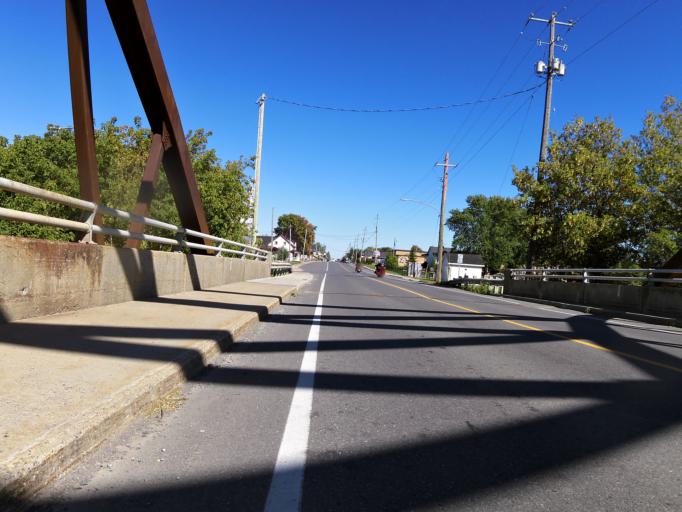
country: CA
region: Ontario
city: Casselman
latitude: 45.2539
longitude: -75.1259
